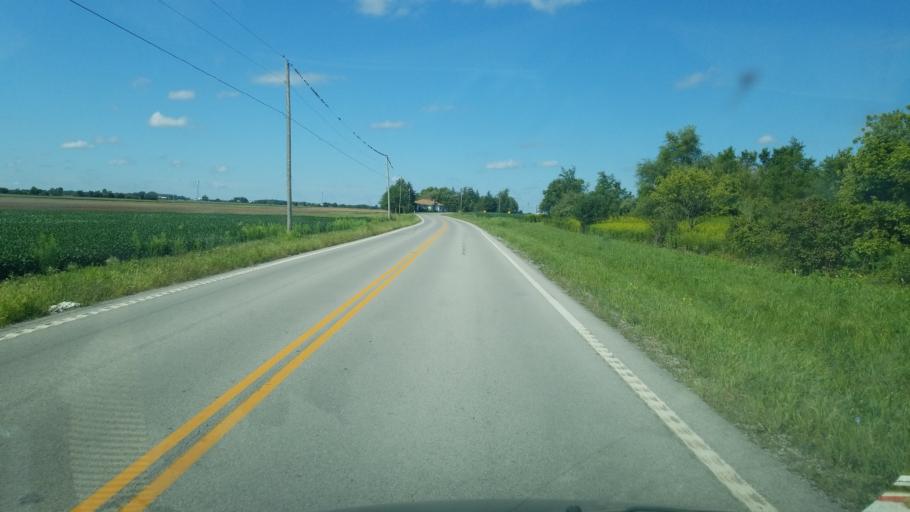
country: US
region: Ohio
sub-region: Wood County
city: North Baltimore
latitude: 41.1254
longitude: -83.7200
